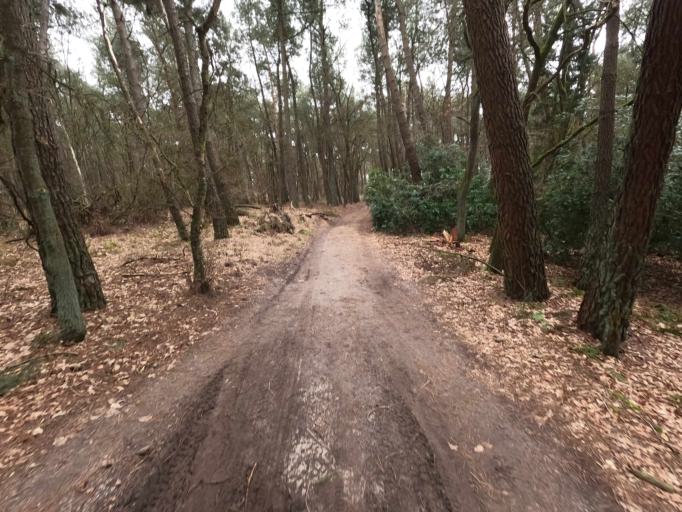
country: BE
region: Flanders
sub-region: Provincie Antwerpen
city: Kalmthout
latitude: 51.4164
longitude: 4.4042
